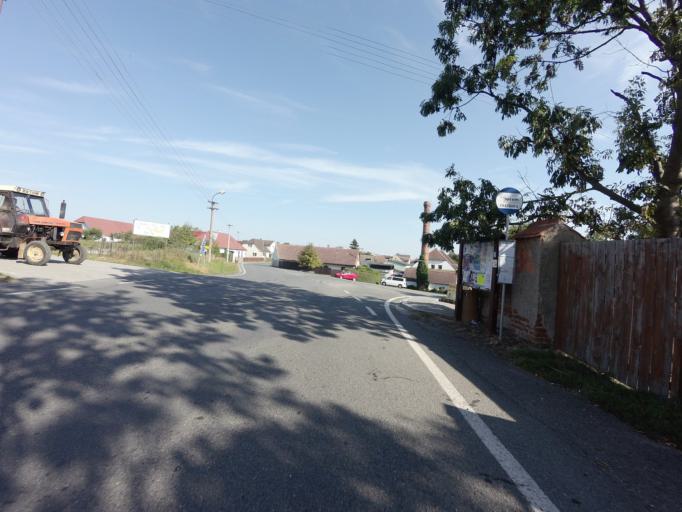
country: CZ
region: Jihocesky
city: Bernartice
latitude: 49.3049
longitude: 14.3808
